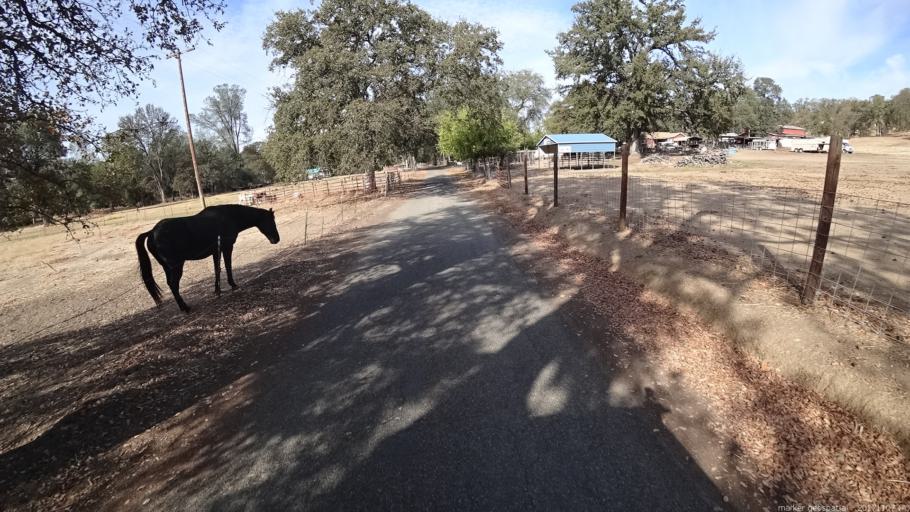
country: US
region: California
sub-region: Shasta County
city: Shasta
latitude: 40.4154
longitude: -122.5274
